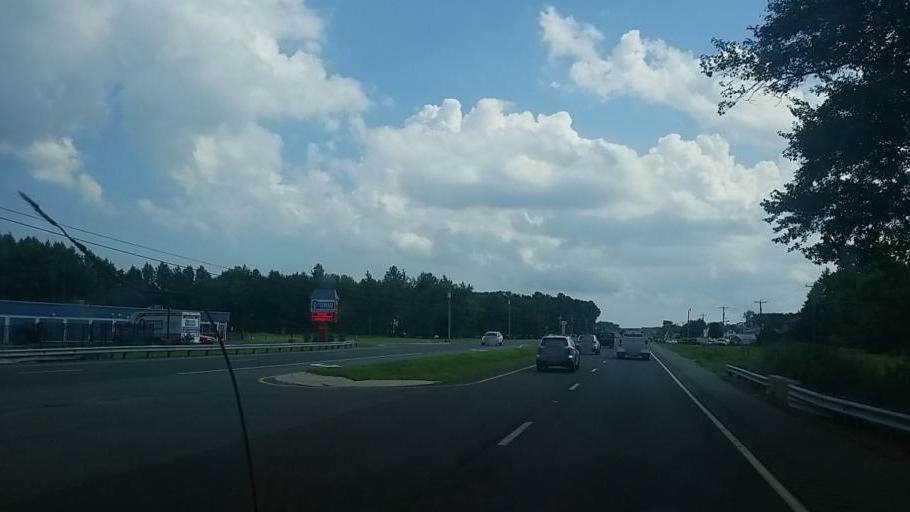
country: US
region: Delaware
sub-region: Sussex County
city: Selbyville
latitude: 38.4694
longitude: -75.2345
